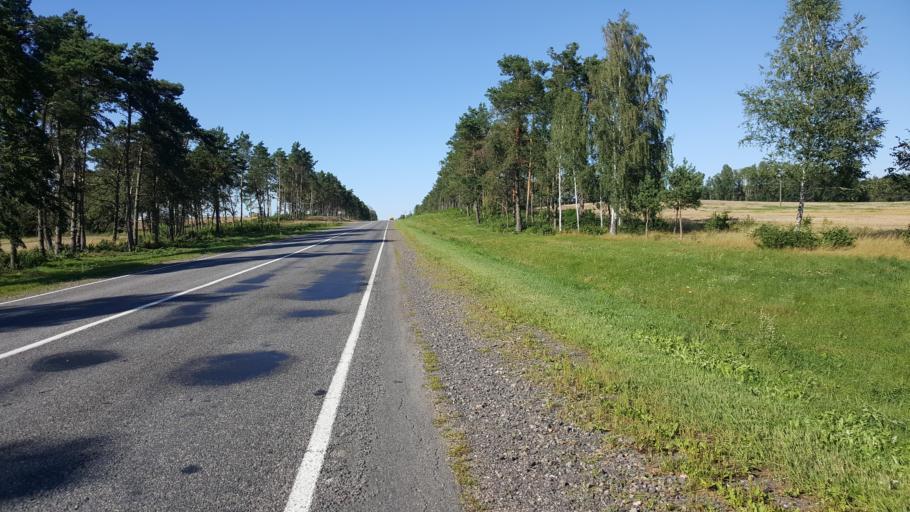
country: BY
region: Brest
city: Charnawchytsy
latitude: 52.2867
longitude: 23.7740
